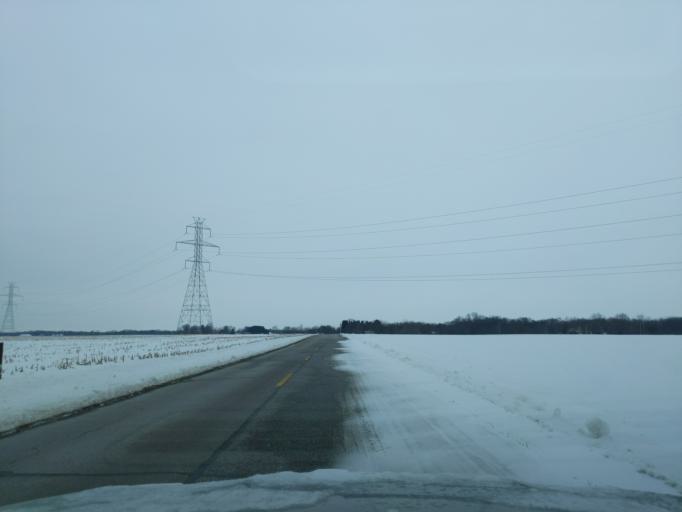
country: US
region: Indiana
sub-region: Benton County
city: Otterbein
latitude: 40.4169
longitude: -87.0885
